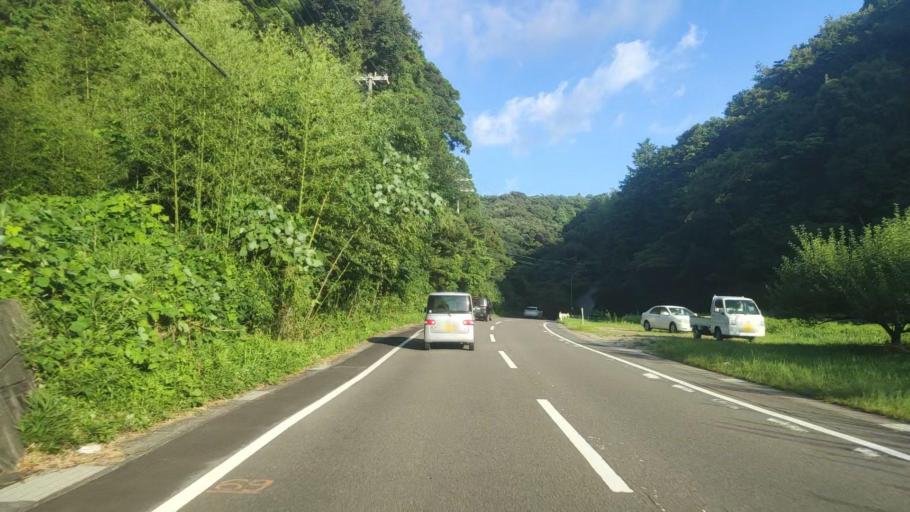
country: JP
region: Wakayama
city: Tanabe
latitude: 33.7317
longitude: 135.4339
